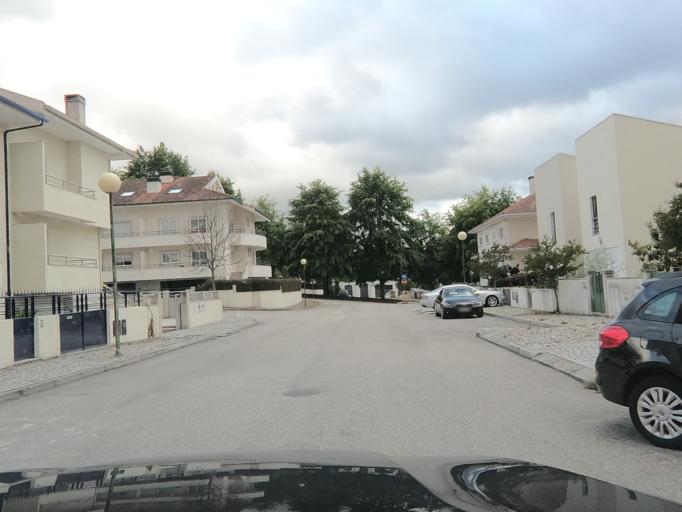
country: PT
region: Vila Real
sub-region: Vila Real
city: Vila Real
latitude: 41.3120
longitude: -7.7210
